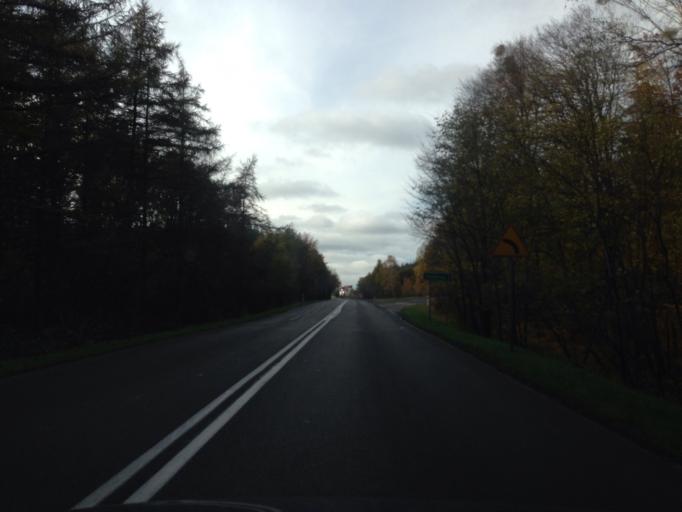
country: PL
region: Kujawsko-Pomorskie
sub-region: Powiat brodnicki
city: Brodnica
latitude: 53.2786
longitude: 19.4473
